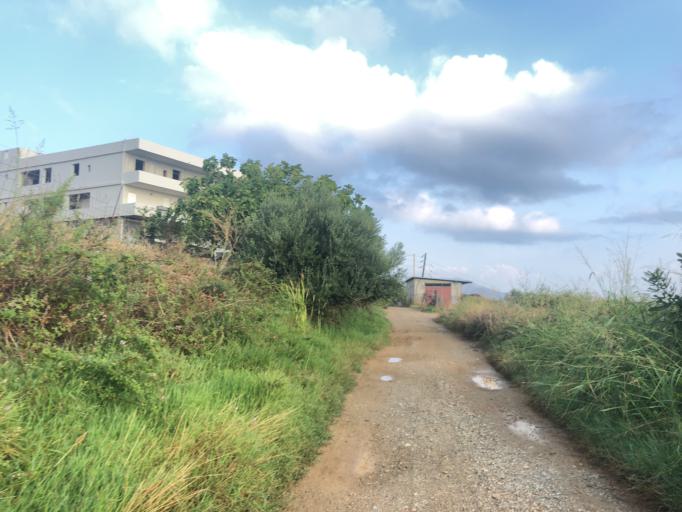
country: GR
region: Crete
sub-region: Nomos Chanias
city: Georgioupolis
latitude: 35.3464
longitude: 24.3120
